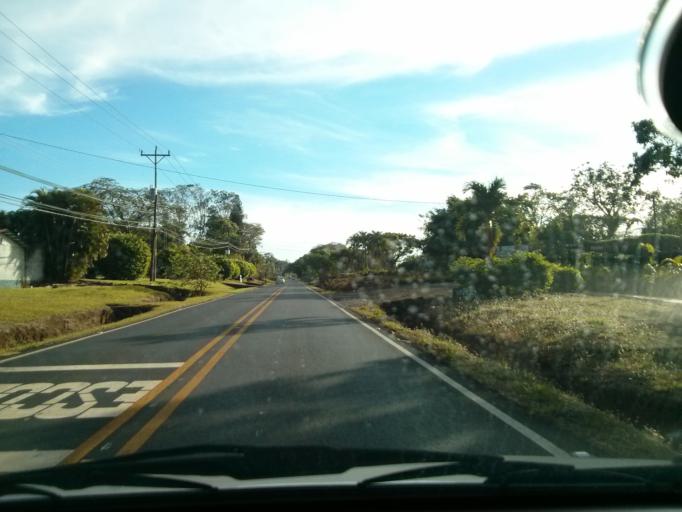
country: CR
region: Alajuela
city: Carrillos
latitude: 10.0098
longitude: -84.2875
